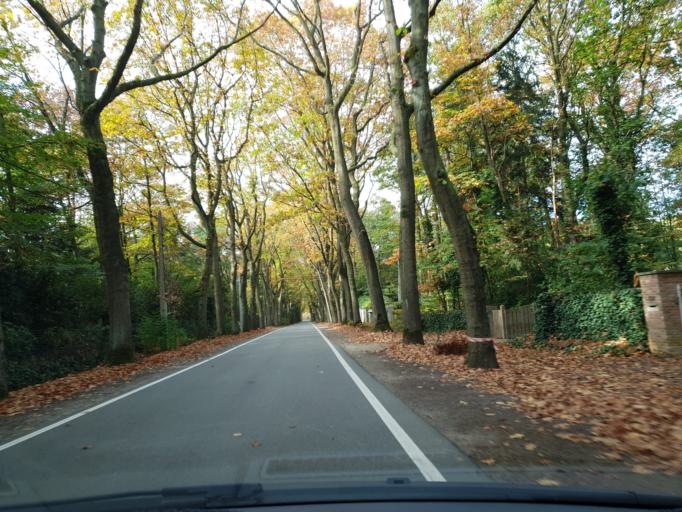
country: BE
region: Flanders
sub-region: Provincie Antwerpen
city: Kalmthout
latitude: 51.3620
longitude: 4.4419
